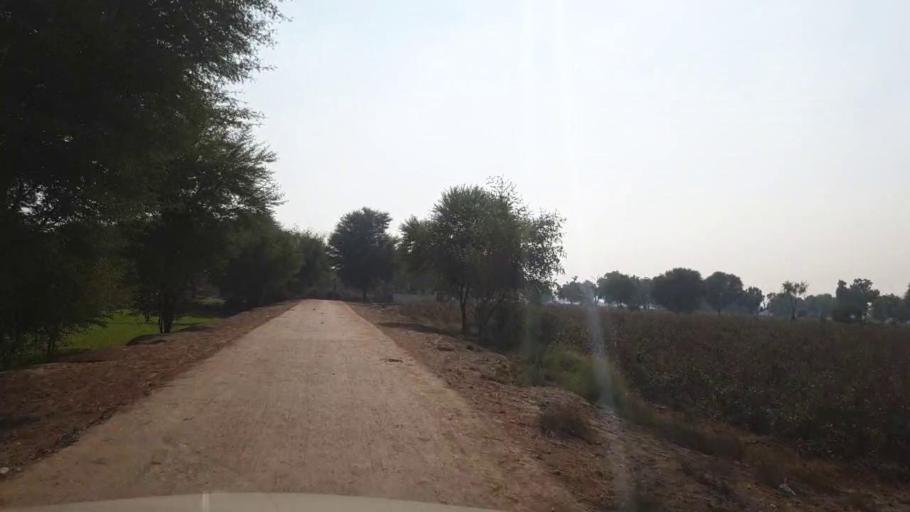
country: PK
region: Sindh
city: Bhan
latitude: 26.5318
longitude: 67.7632
